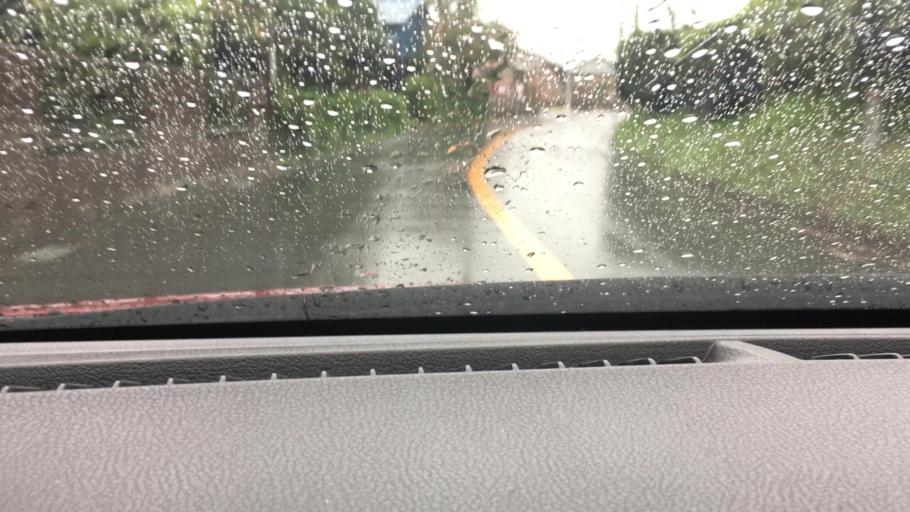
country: JP
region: Chiba
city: Kisarazu
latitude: 35.3732
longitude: 139.9476
